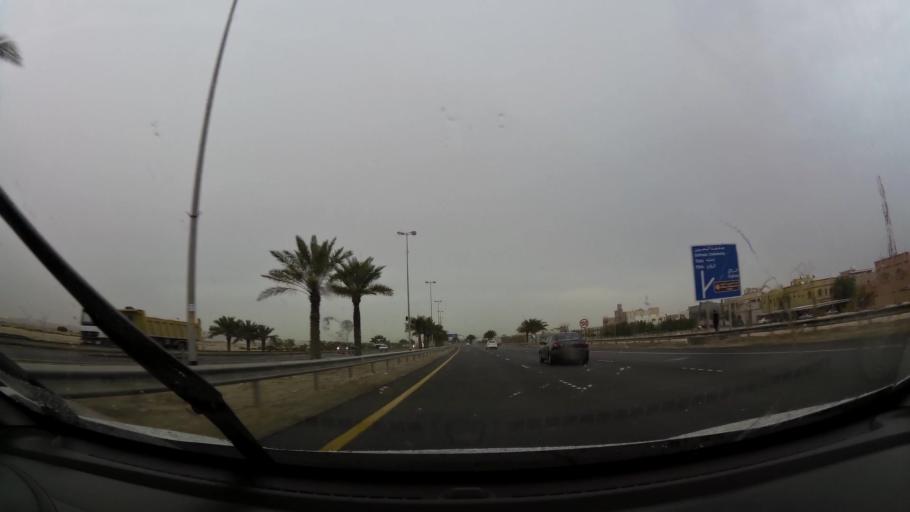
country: BH
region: Central Governorate
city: Dar Kulayb
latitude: 26.0723
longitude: 50.5148
